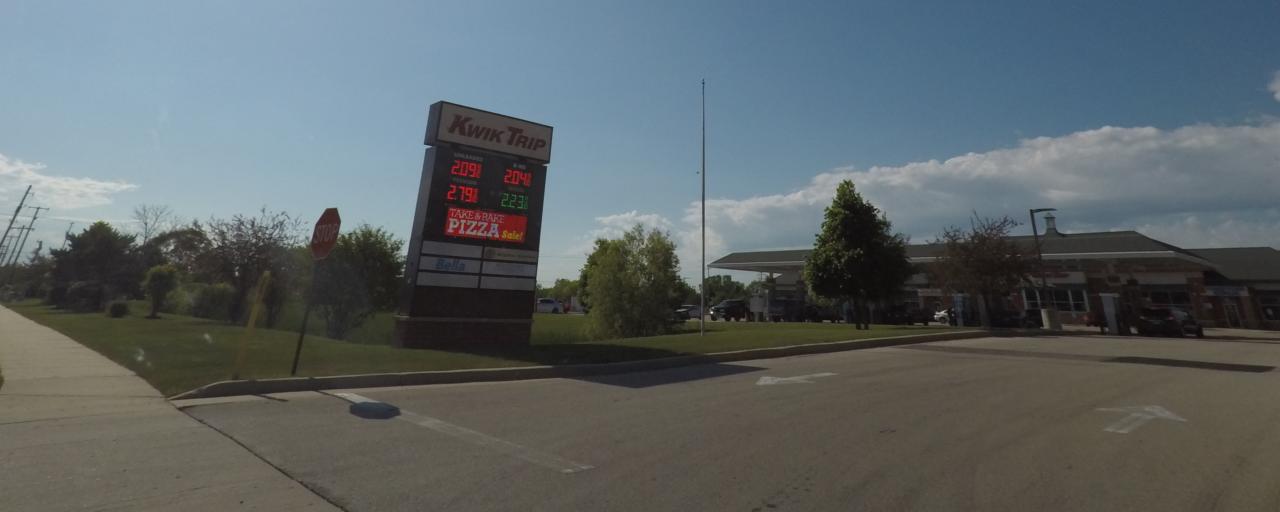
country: US
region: Wisconsin
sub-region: Milwaukee County
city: Greendale
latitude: 42.9164
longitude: -87.9780
